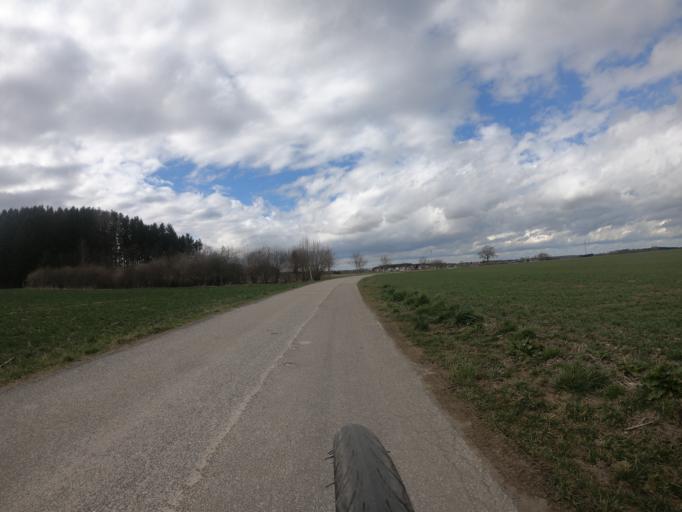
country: DE
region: Bavaria
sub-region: Upper Bavaria
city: Landsberied
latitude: 48.1720
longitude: 11.1974
